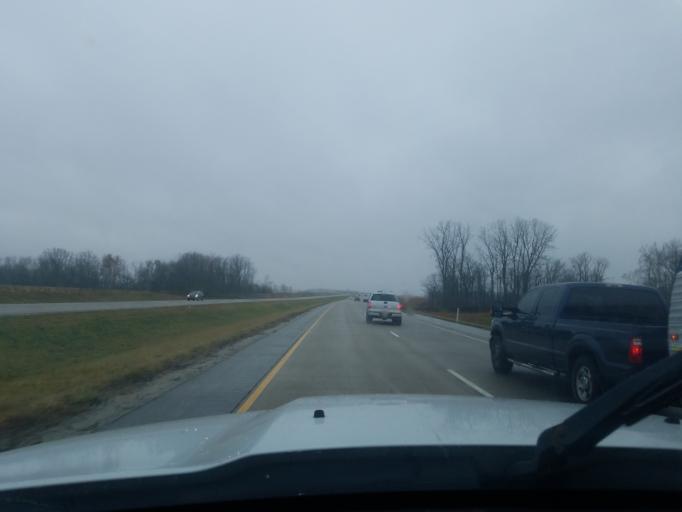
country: US
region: Indiana
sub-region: Howard County
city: Indian Heights
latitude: 40.4303
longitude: -86.0830
